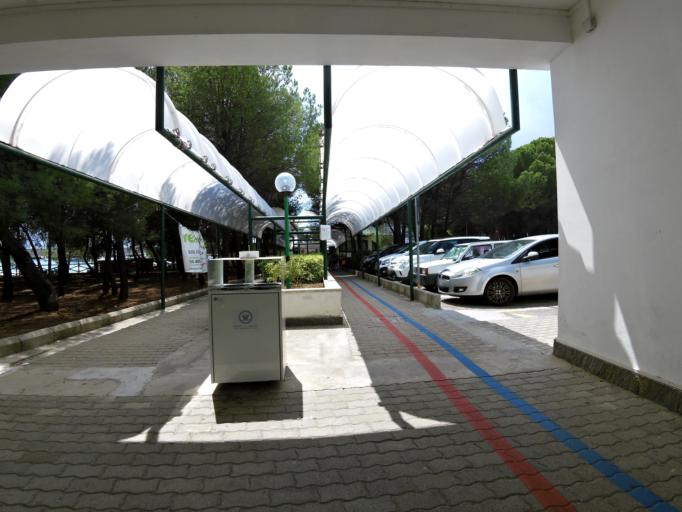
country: IT
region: Calabria
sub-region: Provincia di Reggio Calabria
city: Caulonia Marina
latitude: 38.3295
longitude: 16.4332
